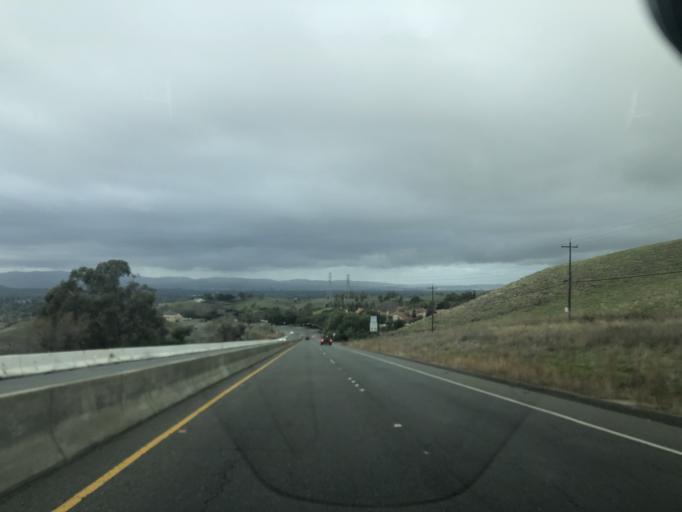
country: US
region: California
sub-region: Contra Costa County
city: Clayton
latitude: 37.9621
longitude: -121.9349
